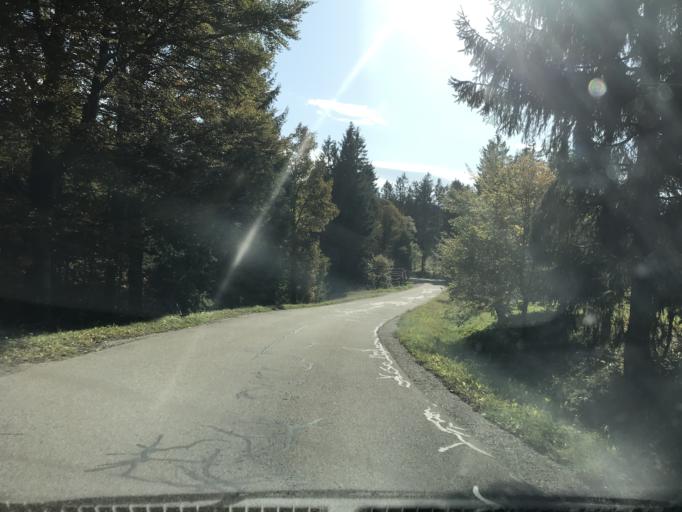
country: DE
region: Baden-Wuerttemberg
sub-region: Freiburg Region
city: Herrischried
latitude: 47.6573
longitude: 7.9671
